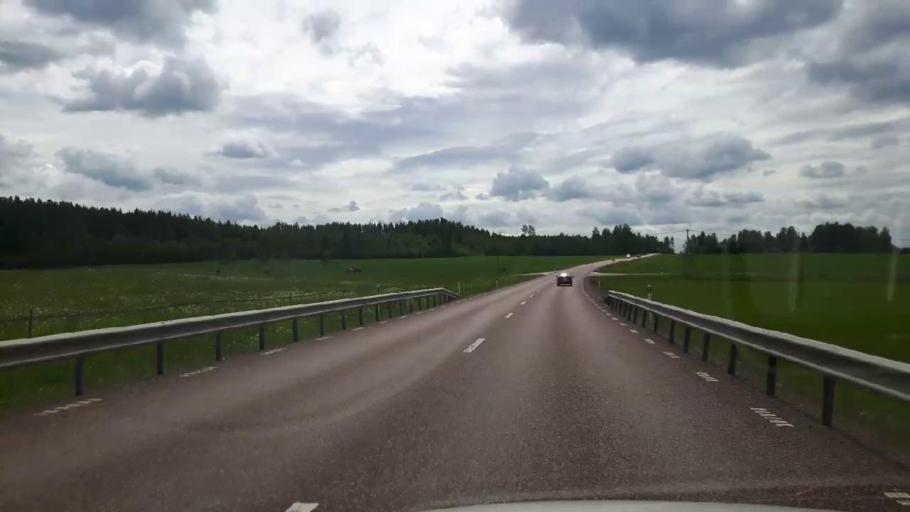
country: SE
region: Dalarna
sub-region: Hedemora Kommun
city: Hedemora
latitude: 60.3431
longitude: 15.9457
